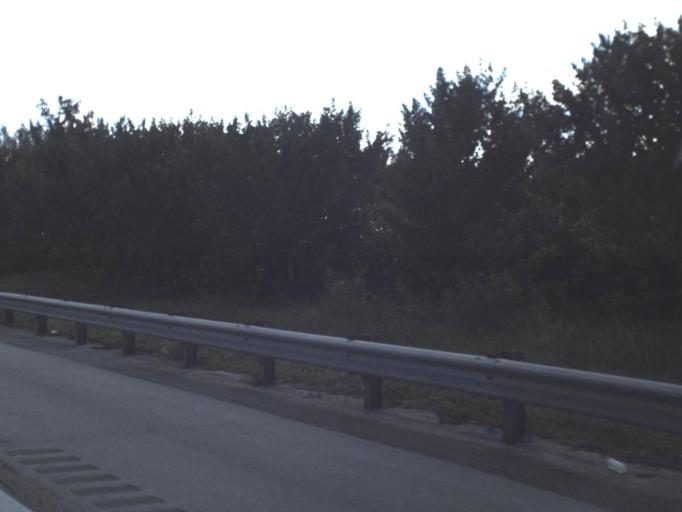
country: US
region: Florida
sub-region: Palm Beach County
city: Boca Del Mar
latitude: 26.3590
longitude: -80.1708
